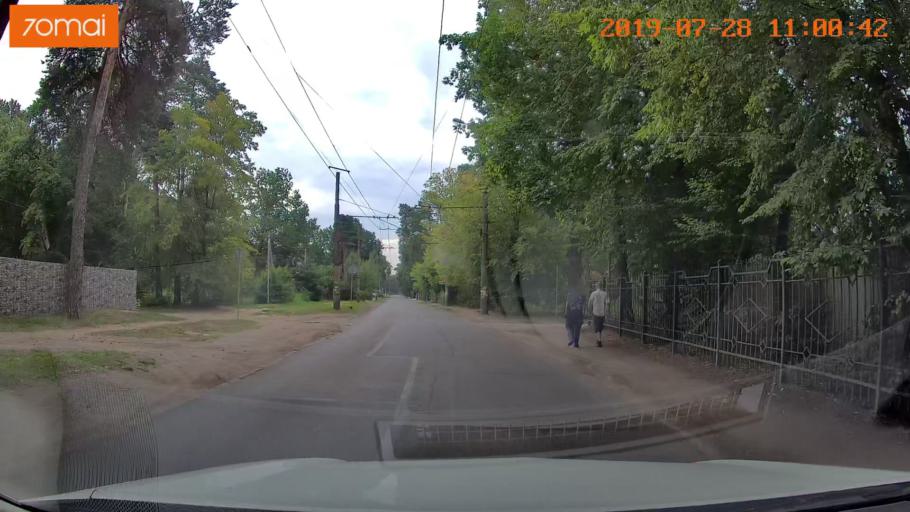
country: RU
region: Kaliningrad
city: Vzmorye
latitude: 54.7257
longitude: 20.3631
